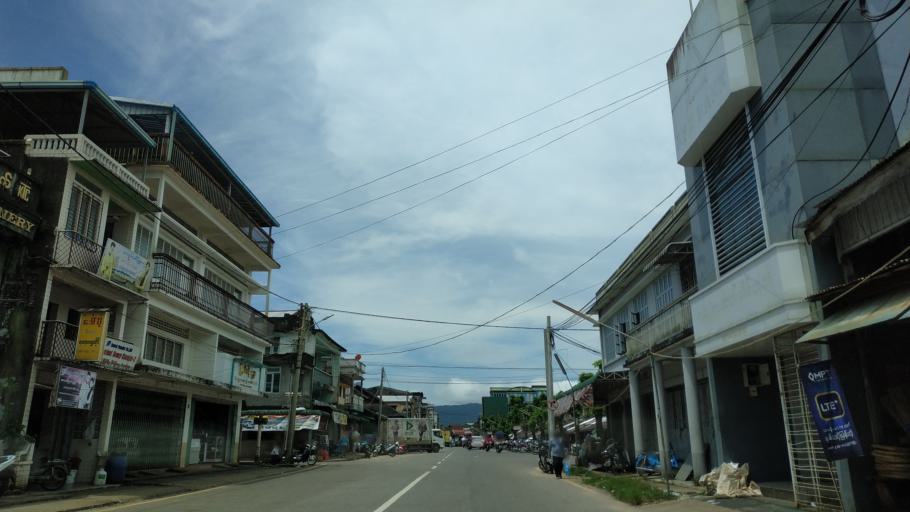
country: MM
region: Tanintharyi
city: Dawei
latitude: 14.0721
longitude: 98.1923
